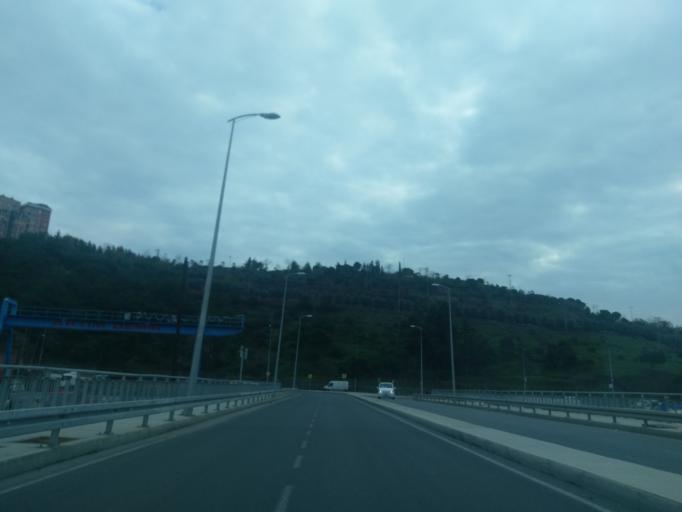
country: TR
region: Istanbul
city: Sisli
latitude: 41.0912
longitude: 28.9837
